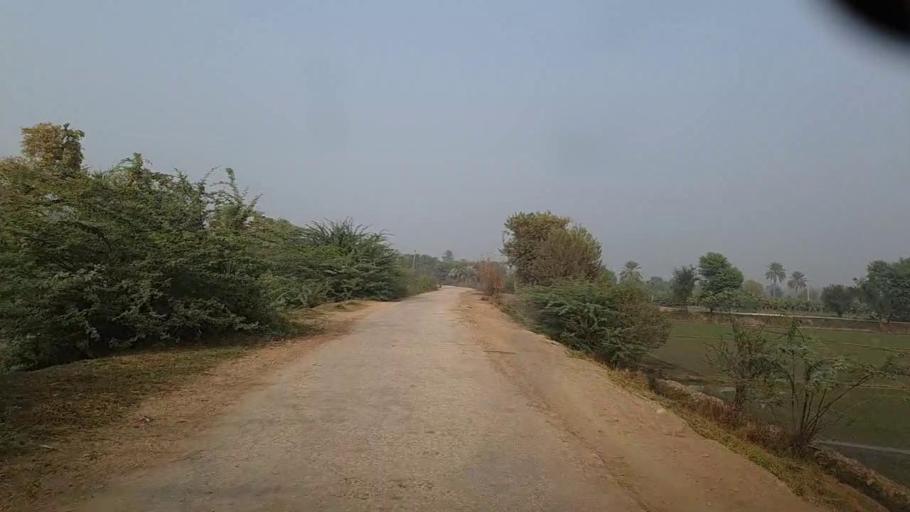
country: PK
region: Sindh
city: Bozdar
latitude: 27.1654
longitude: 68.6622
